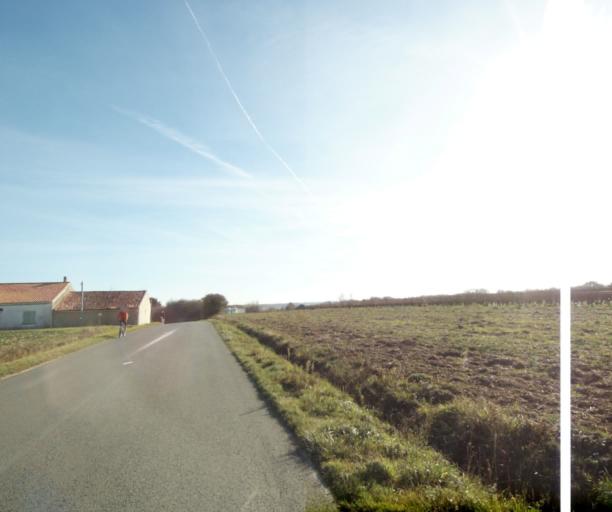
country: FR
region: Poitou-Charentes
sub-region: Departement de la Charente-Maritime
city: Chaniers
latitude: 45.7532
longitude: -0.5162
